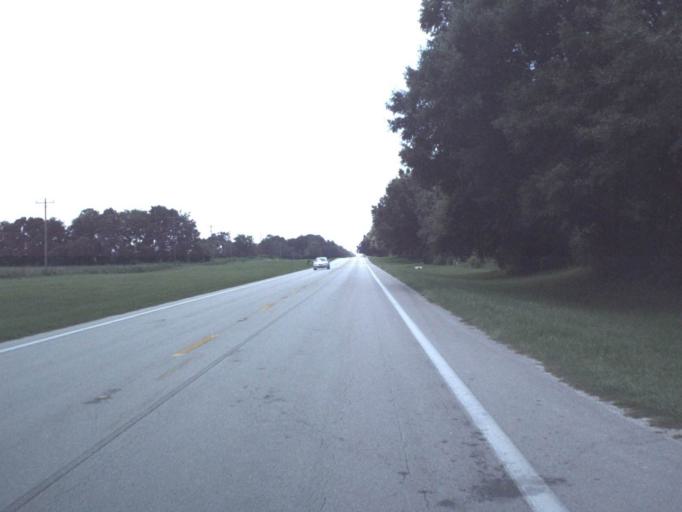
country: US
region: Florida
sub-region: Alachua County
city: Newberry
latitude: 29.7046
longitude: -82.6071
